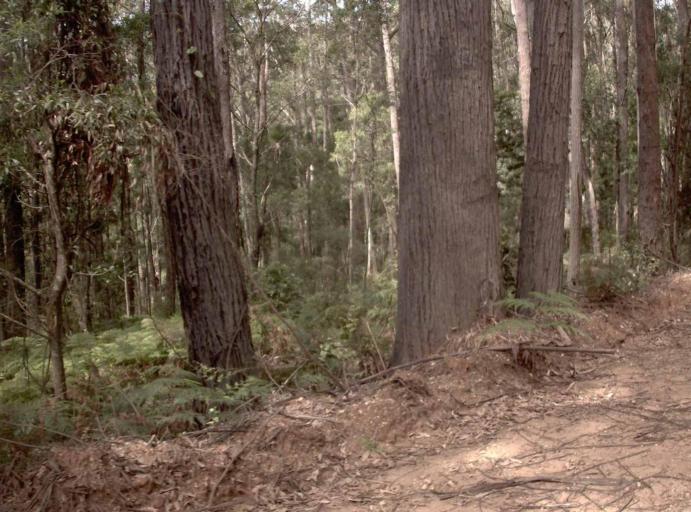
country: AU
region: Victoria
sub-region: East Gippsland
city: Lakes Entrance
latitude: -37.6207
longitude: 148.6893
